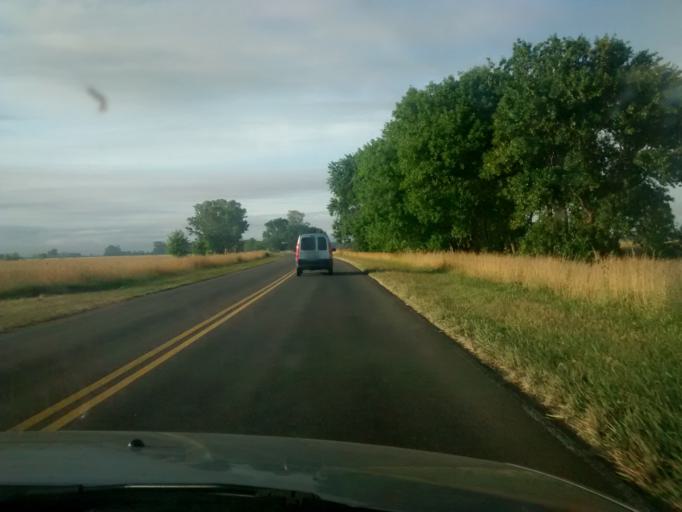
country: AR
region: Buenos Aires
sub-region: Partido de Brandsen
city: Brandsen
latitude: -35.2940
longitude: -58.2343
